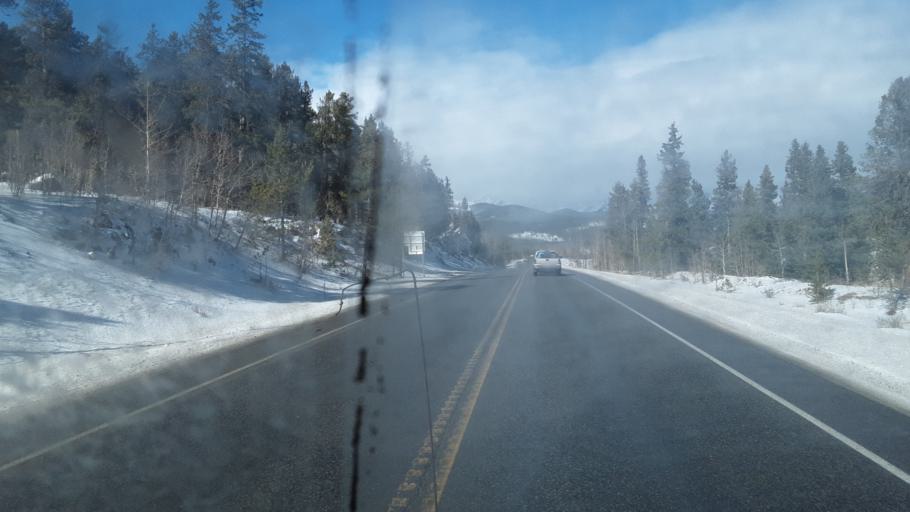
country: US
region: Colorado
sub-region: Summit County
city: Breckenridge
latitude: 39.4138
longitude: -105.7594
